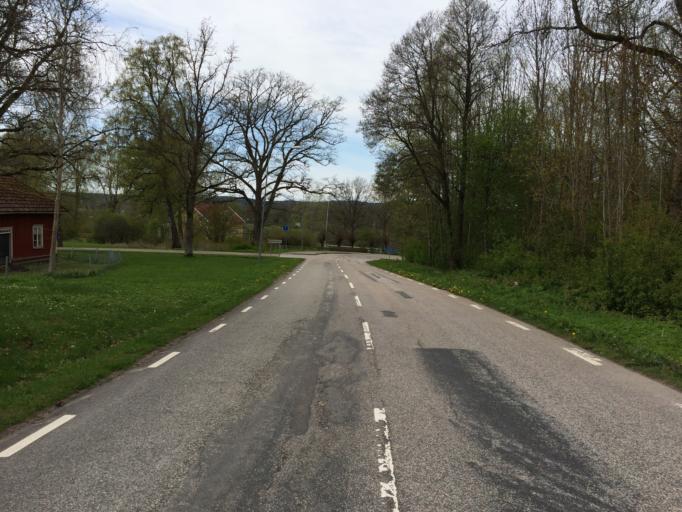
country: SE
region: Vaestra Goetaland
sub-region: Ulricehamns Kommun
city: Ulricehamn
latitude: 57.7343
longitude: 13.4274
